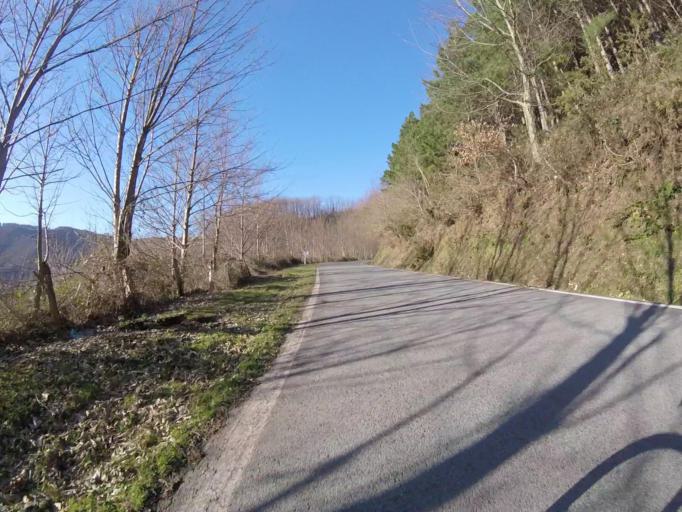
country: ES
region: Navarre
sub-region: Provincia de Navarra
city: Lesaka
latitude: 43.2635
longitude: -1.7379
